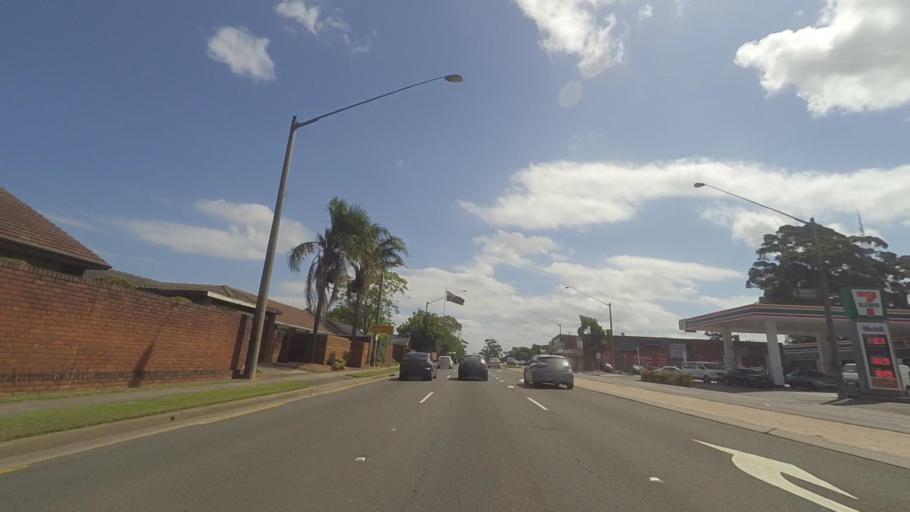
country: AU
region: New South Wales
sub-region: The Hills Shire
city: West Pennant
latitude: -33.7469
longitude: 151.0513
